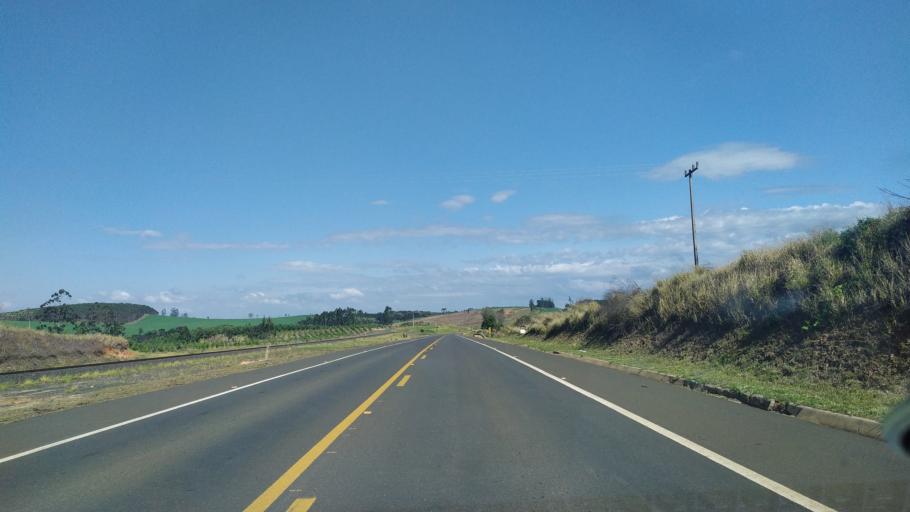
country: BR
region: Parana
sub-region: Ortigueira
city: Ortigueira
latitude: -24.2780
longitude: -50.8073
